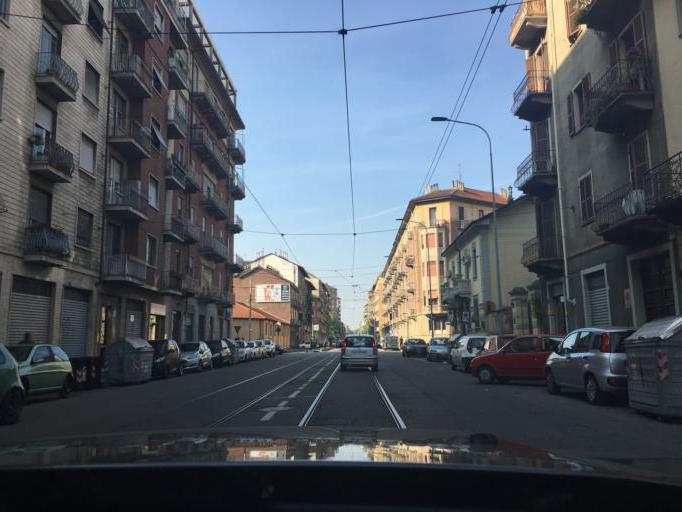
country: IT
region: Piedmont
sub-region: Provincia di Torino
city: Turin
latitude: 45.0819
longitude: 7.6928
